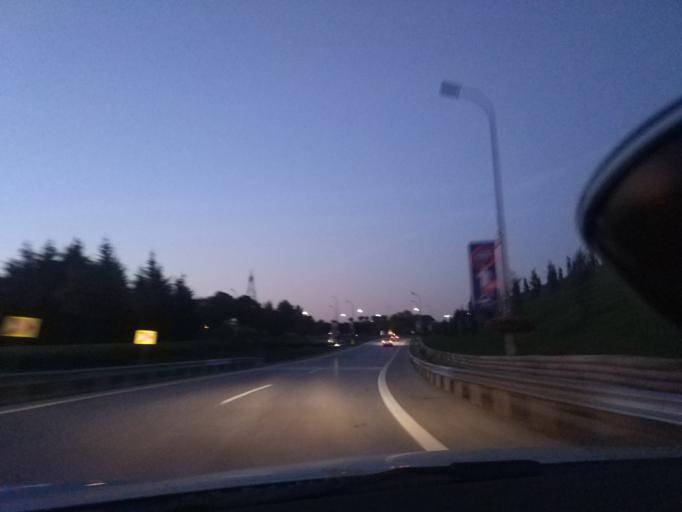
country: TR
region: Istanbul
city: Pendik
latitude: 40.9164
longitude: 29.3226
